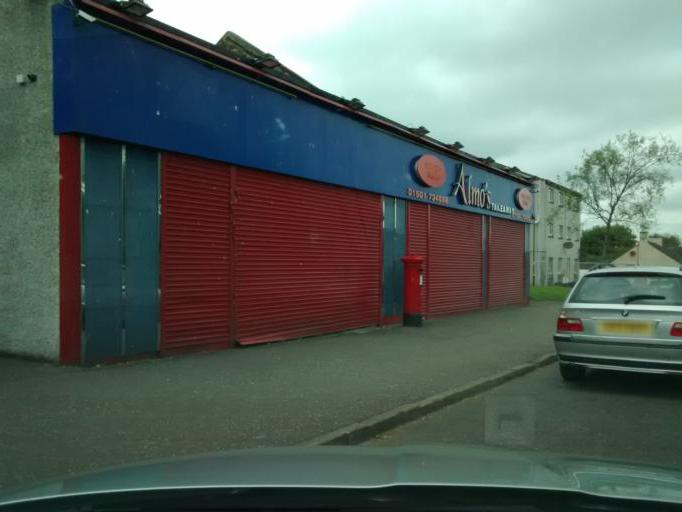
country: GB
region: Scotland
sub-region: West Lothian
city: Armadale
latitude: 55.8918
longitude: -3.7010
